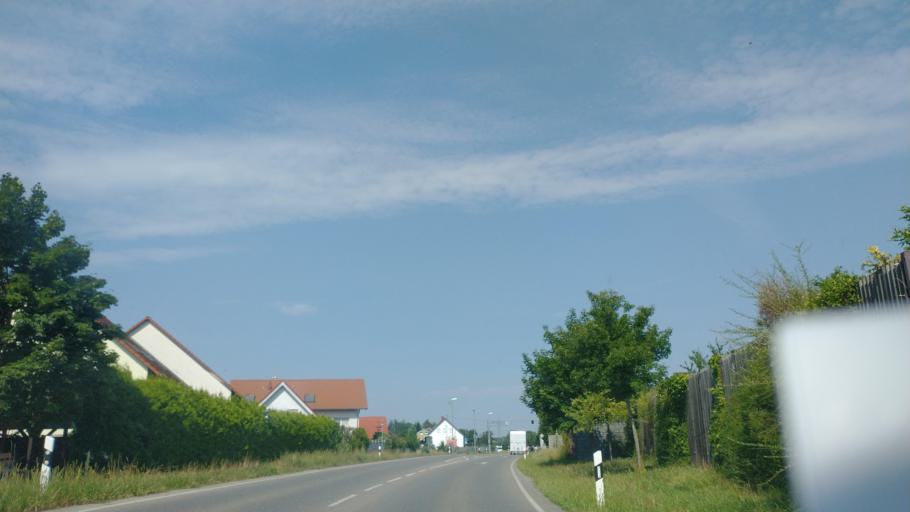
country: DE
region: Baden-Wuerttemberg
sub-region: Tuebingen Region
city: Meckenbeuren
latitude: 47.6690
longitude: 9.5555
